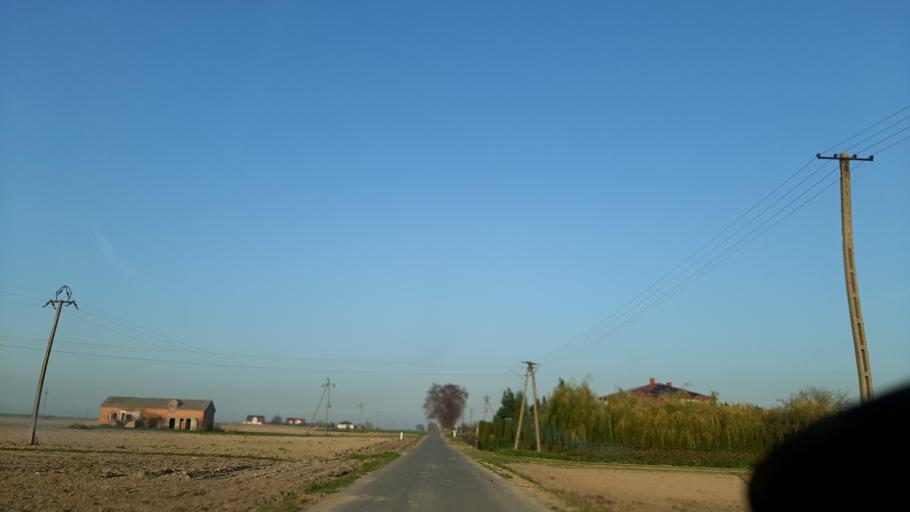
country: PL
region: Lublin Voivodeship
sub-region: Powiat lubelski
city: Garbow
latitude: 51.3767
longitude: 22.3317
